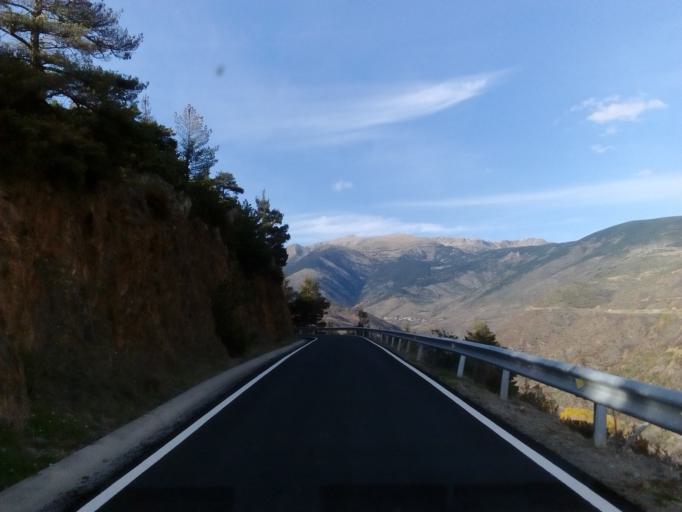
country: ES
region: Catalonia
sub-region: Provincia de Lleida
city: Eller
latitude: 42.4079
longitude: 1.8004
